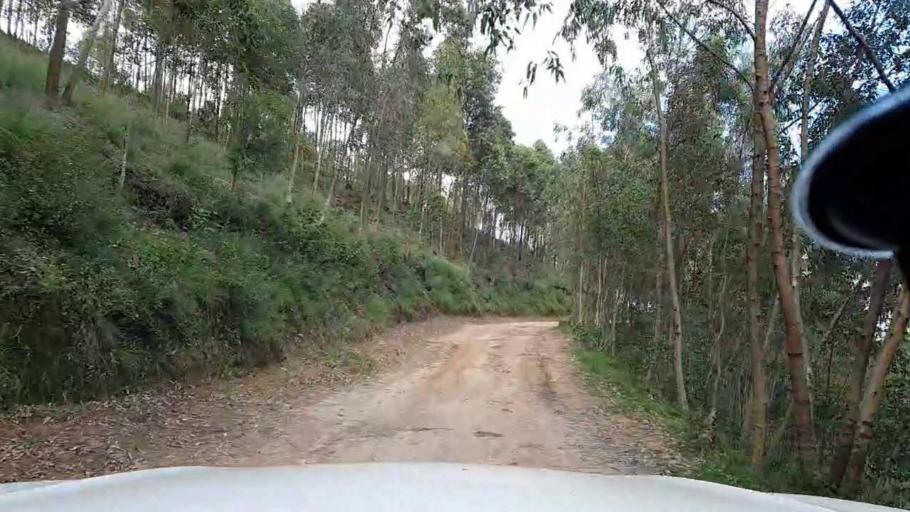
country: RW
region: Kigali
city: Kigali
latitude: -1.7832
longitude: 29.8339
